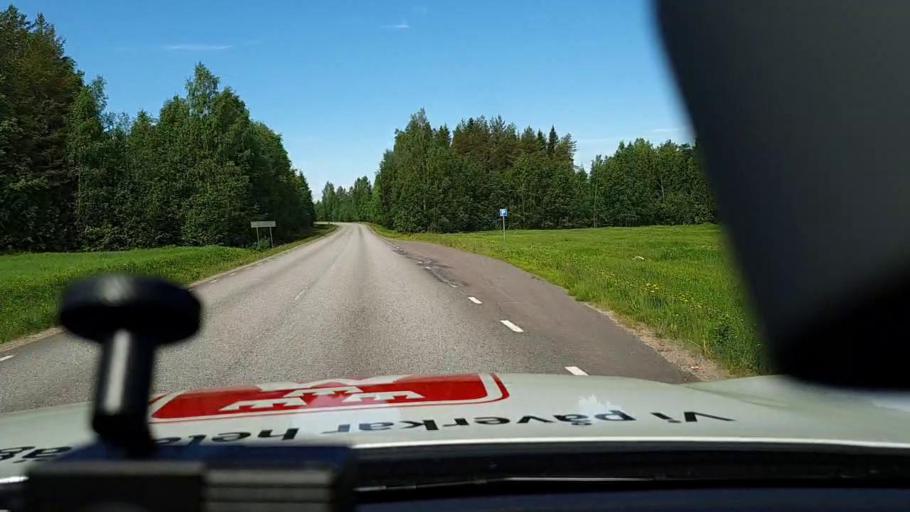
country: SE
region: Norrbotten
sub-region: Lulea Kommun
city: Sodra Sunderbyn
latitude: 65.6578
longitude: 21.8428
